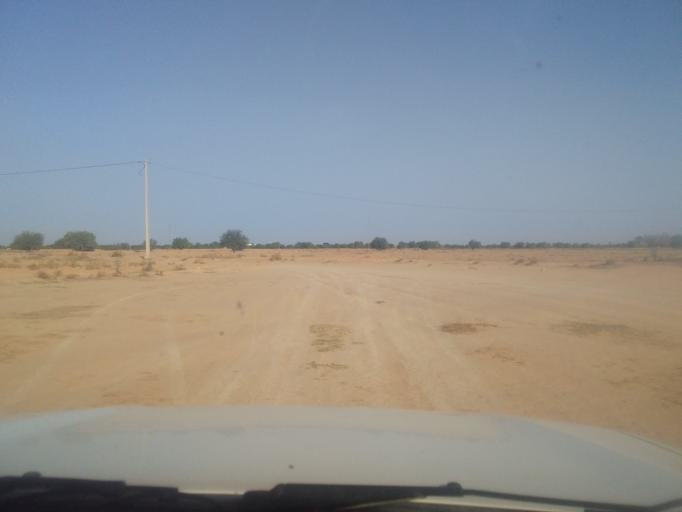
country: TN
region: Qabis
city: Matmata
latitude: 33.5847
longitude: 10.2718
